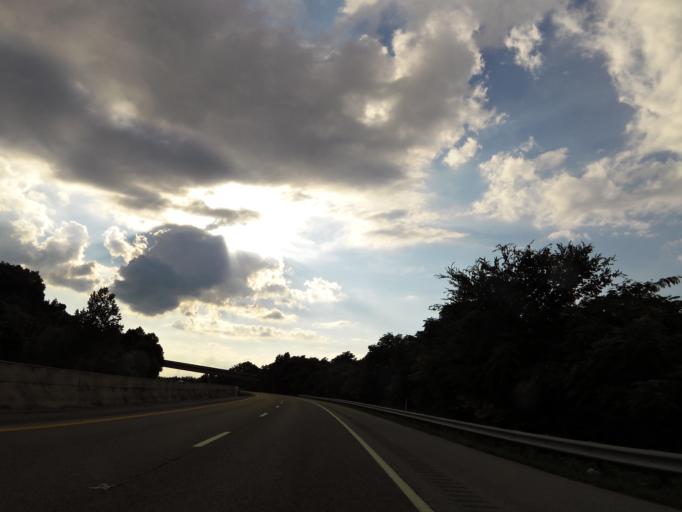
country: US
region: Tennessee
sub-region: Blount County
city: Louisville
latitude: 35.8661
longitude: -84.0360
